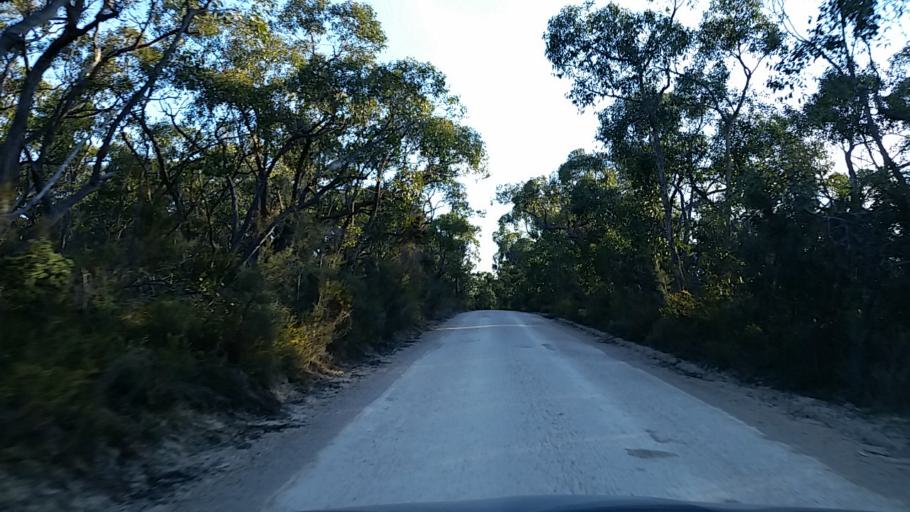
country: AU
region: South Australia
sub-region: Alexandrina
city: Mount Compass
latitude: -35.3067
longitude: 138.6745
